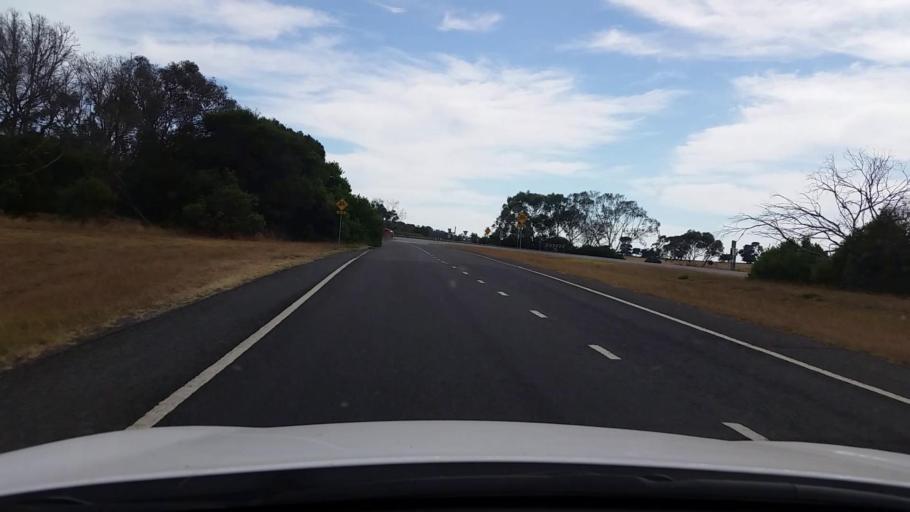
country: AU
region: Victoria
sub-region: Mornington Peninsula
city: Safety Beach
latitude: -38.2994
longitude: 145.0317
